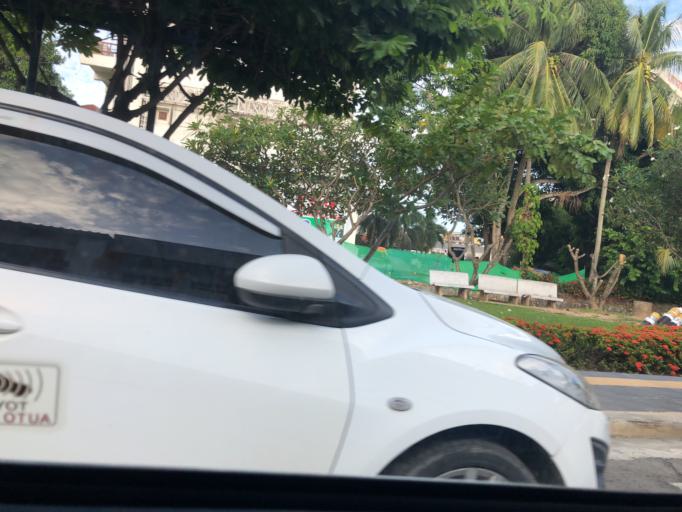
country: TH
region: Phuket
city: Ban Talat Nua
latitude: 7.8834
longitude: 98.3908
